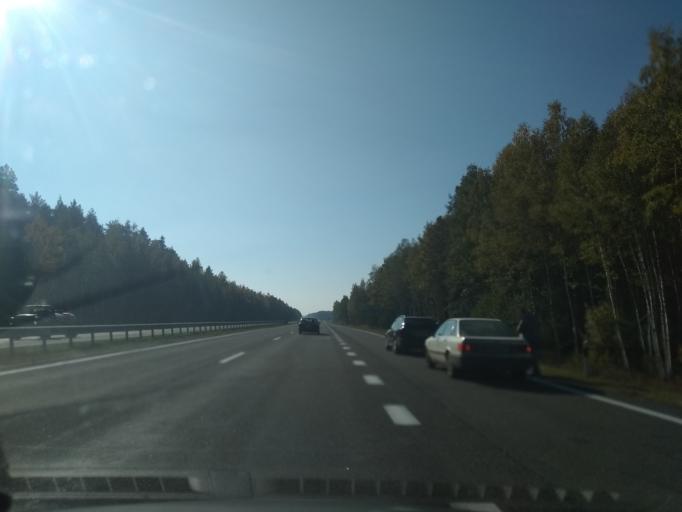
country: BY
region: Brest
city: Ivatsevichy
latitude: 52.8192
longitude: 25.5856
